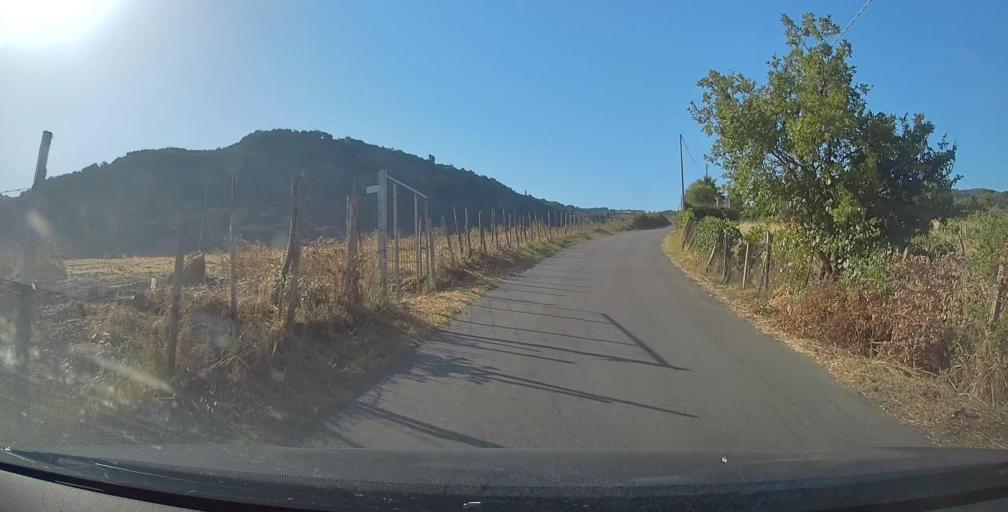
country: IT
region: Sicily
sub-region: Messina
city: San Piero Patti
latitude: 38.0683
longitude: 14.9874
